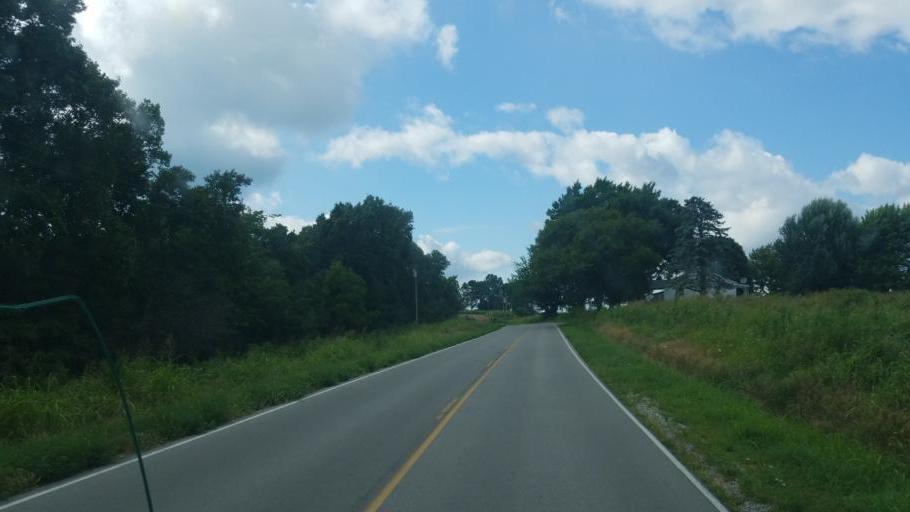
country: US
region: Illinois
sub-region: Union County
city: Cobden
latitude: 37.5529
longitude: -89.2959
